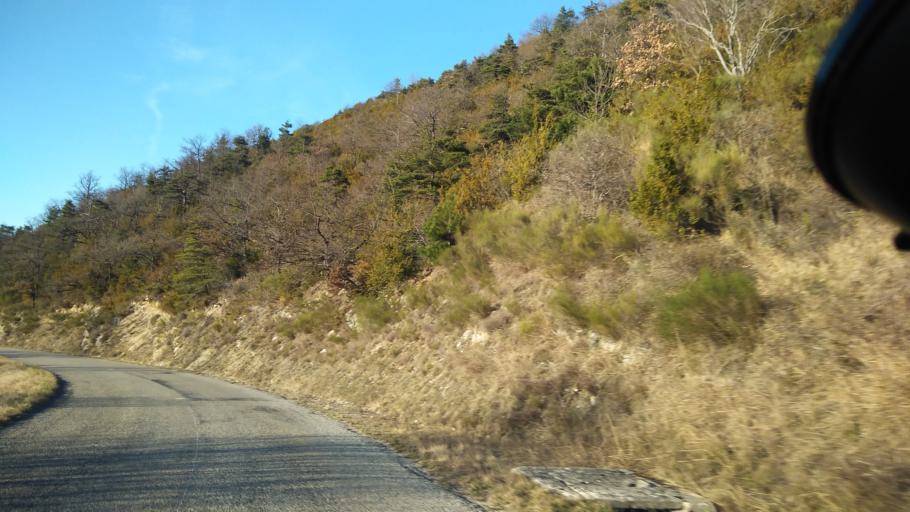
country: FR
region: Rhone-Alpes
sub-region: Departement de la Drome
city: Chabeuil
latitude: 44.8477
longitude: 5.0897
